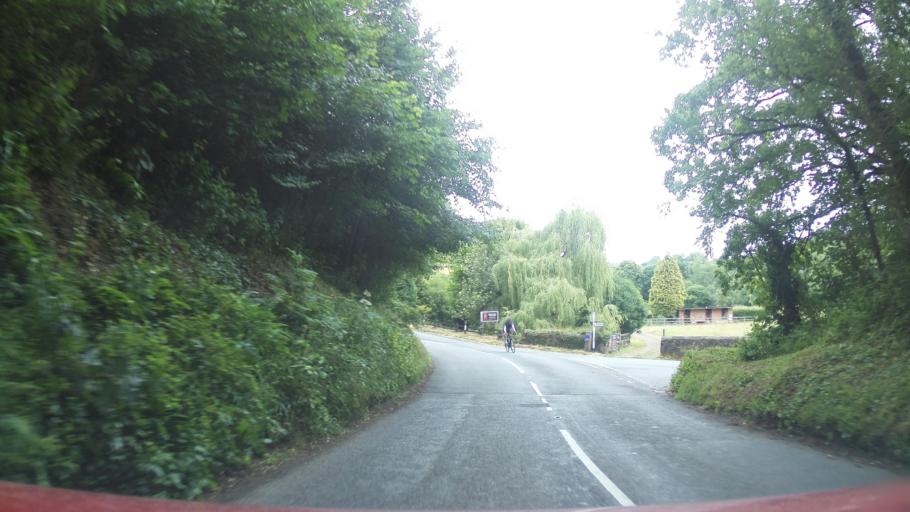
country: GB
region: England
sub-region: Devon
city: Chudleigh
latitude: 50.6182
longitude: -3.6301
